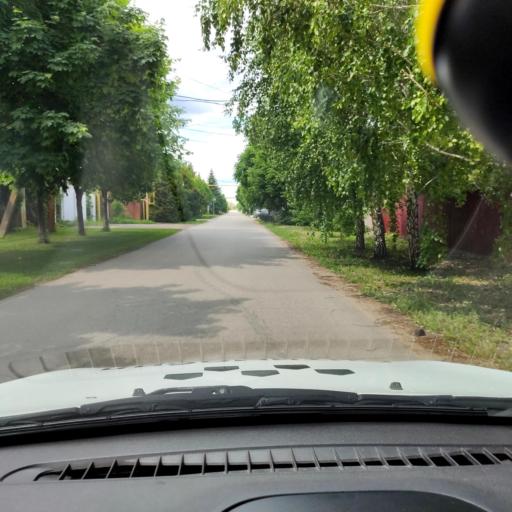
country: RU
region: Samara
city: Podstepki
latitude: 53.5167
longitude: 49.1700
